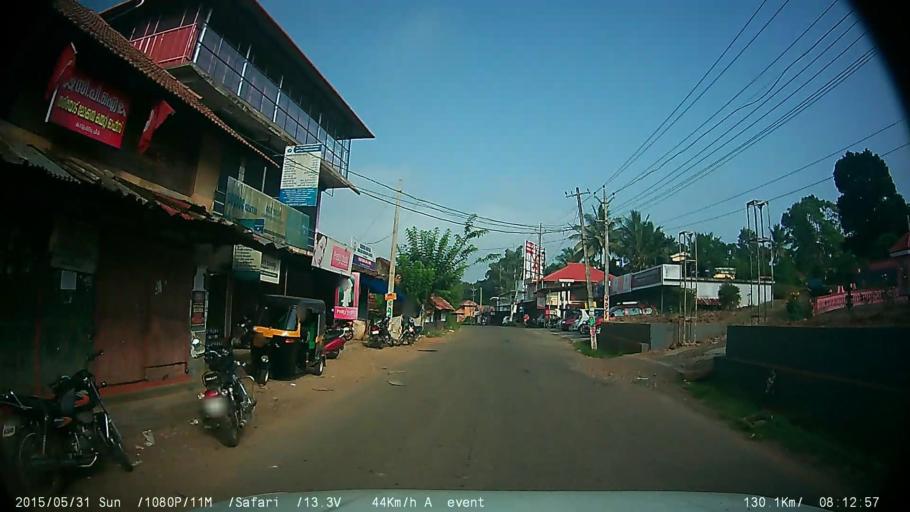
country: IN
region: Kerala
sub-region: Wayanad
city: Kalpetta
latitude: 11.6379
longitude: 76.0107
